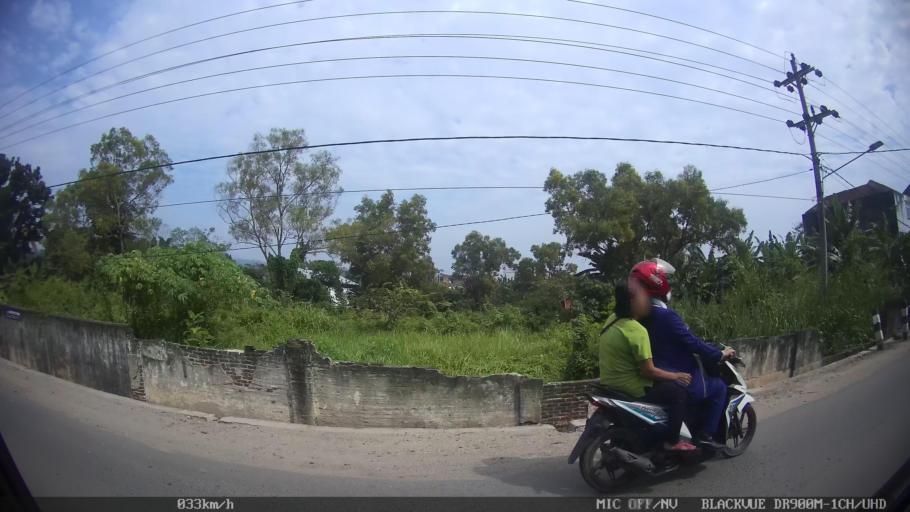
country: ID
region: Lampung
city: Bandarlampung
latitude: -5.4573
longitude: 105.2541
